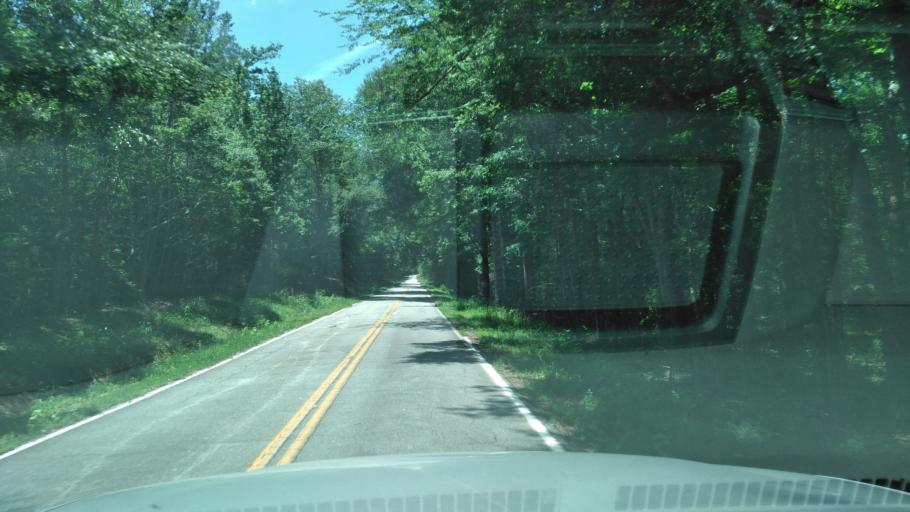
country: US
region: South Carolina
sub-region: Greenwood County
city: Ware Shoals
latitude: 34.3827
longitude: -82.1066
